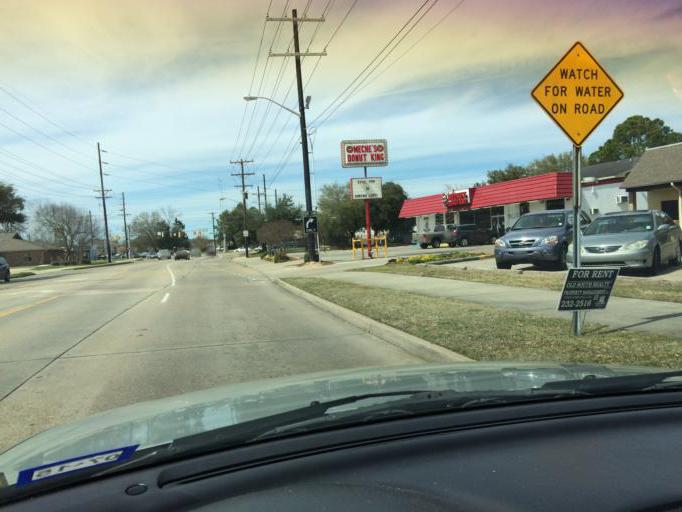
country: US
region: Louisiana
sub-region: Lafayette Parish
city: Scott
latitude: 30.1974
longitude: -92.0687
